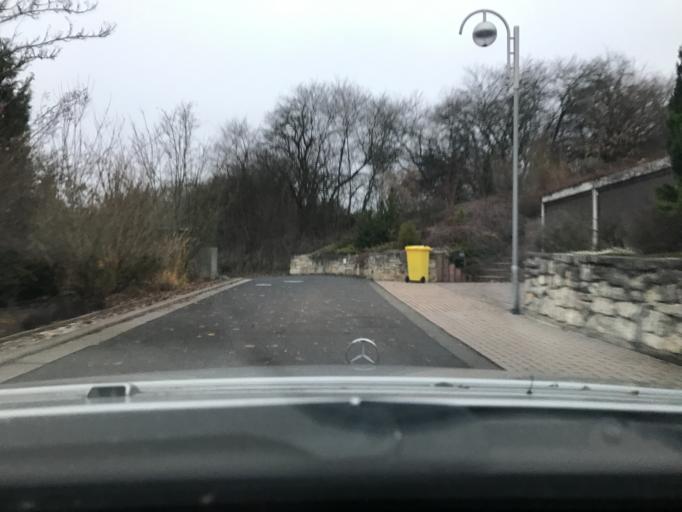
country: DE
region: Thuringia
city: Muehlhausen
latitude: 51.2363
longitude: 10.4389
